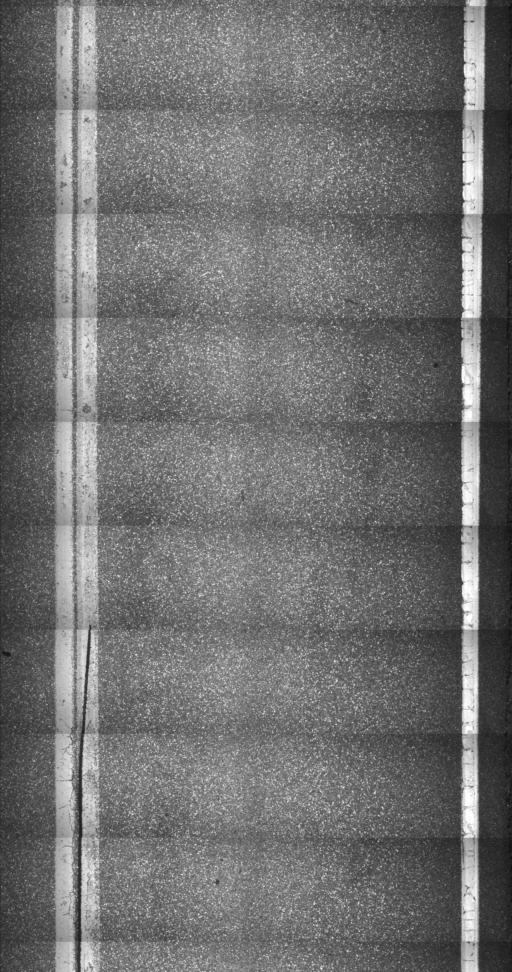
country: US
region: Vermont
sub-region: Windsor County
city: Wilder
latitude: 43.7202
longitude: -72.4192
